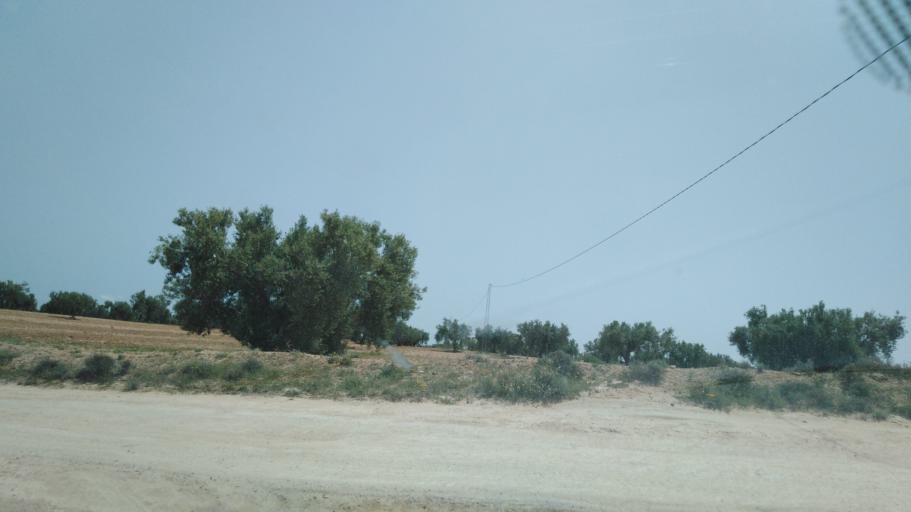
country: TN
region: Safaqis
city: Sfax
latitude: 34.7199
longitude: 10.5703
